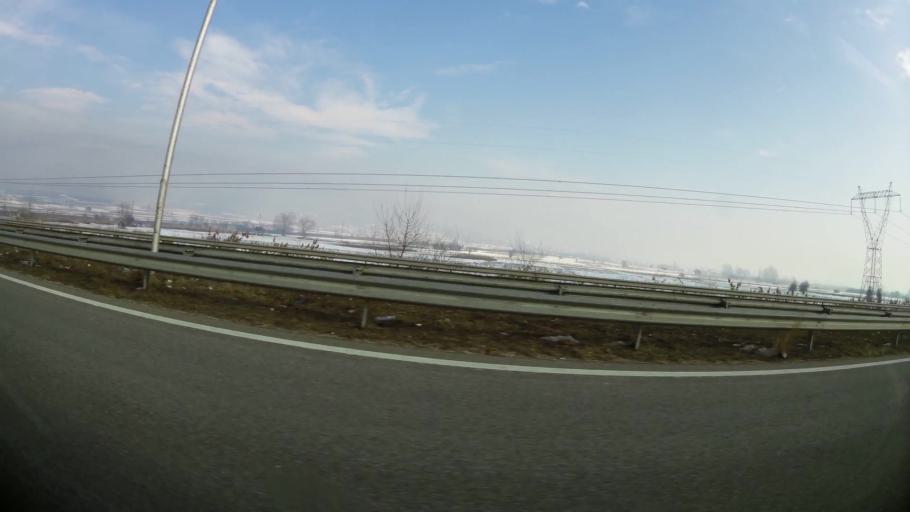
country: MK
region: Aracinovo
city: Arachinovo
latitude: 42.0251
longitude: 21.5312
